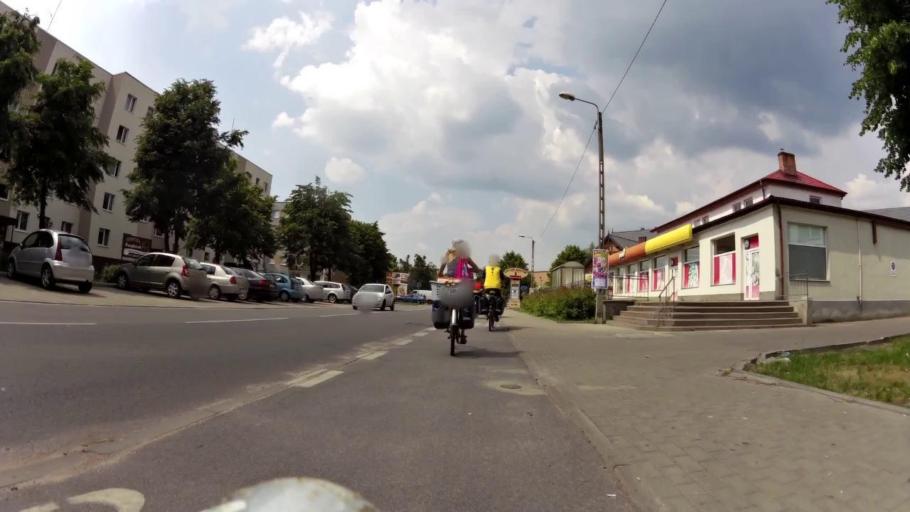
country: PL
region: Kujawsko-Pomorskie
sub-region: Powiat bydgoski
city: Koronowo
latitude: 53.3086
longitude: 17.9417
